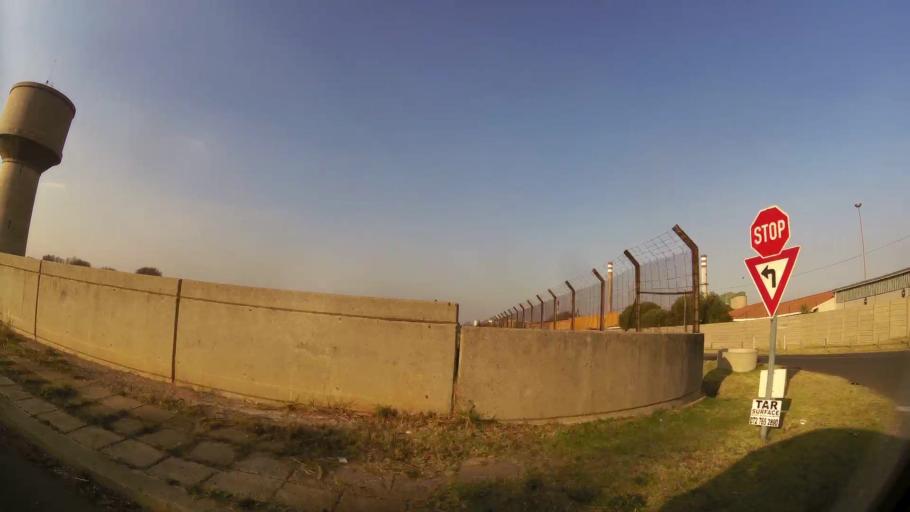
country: ZA
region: Gauteng
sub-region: Ekurhuleni Metropolitan Municipality
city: Springs
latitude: -26.2588
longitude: 28.4060
